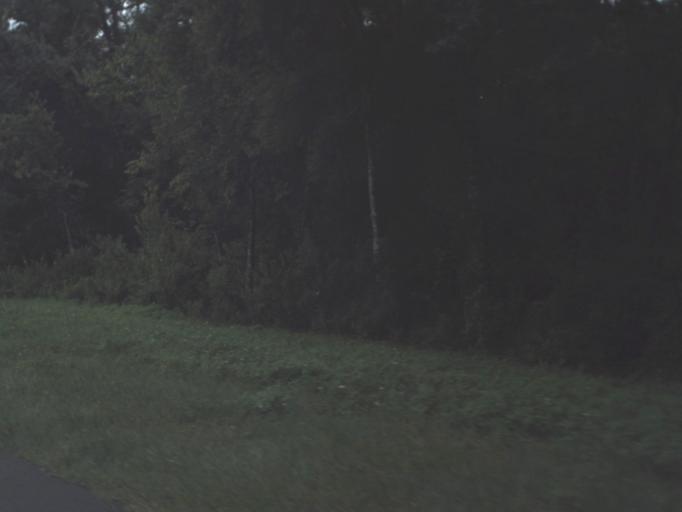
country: US
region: Florida
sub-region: Pasco County
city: Zephyrhills North
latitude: 28.2672
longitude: -82.0900
